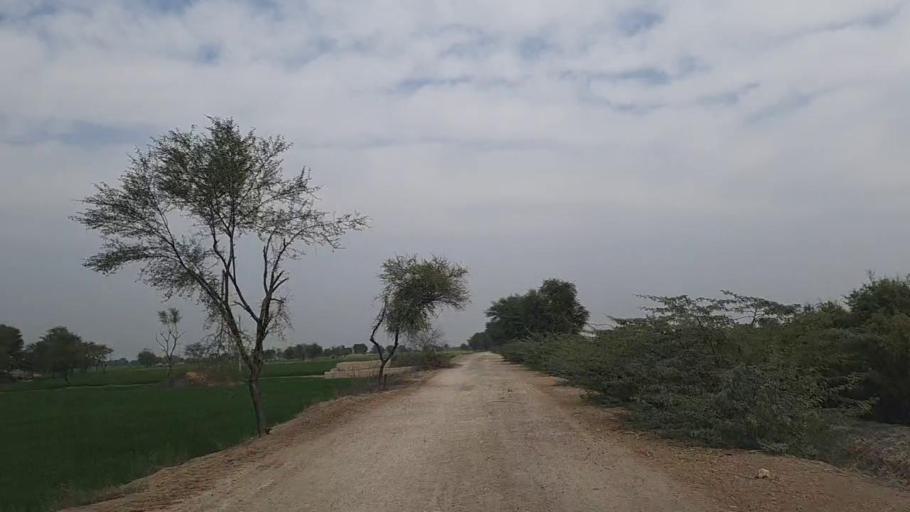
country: PK
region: Sindh
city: Daur
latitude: 26.4280
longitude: 68.4625
